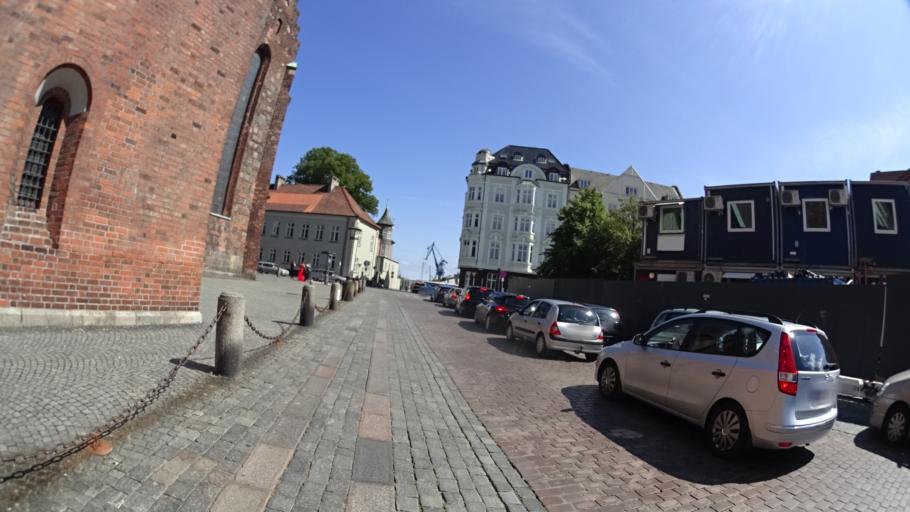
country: DK
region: Central Jutland
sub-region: Arhus Kommune
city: Arhus
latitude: 56.1566
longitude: 10.2107
